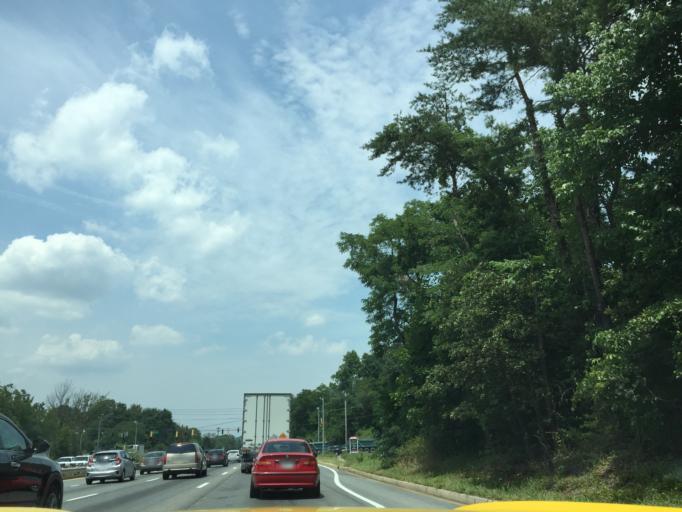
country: US
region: Maryland
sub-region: Prince George's County
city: Friendly
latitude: 38.7546
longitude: -76.9929
